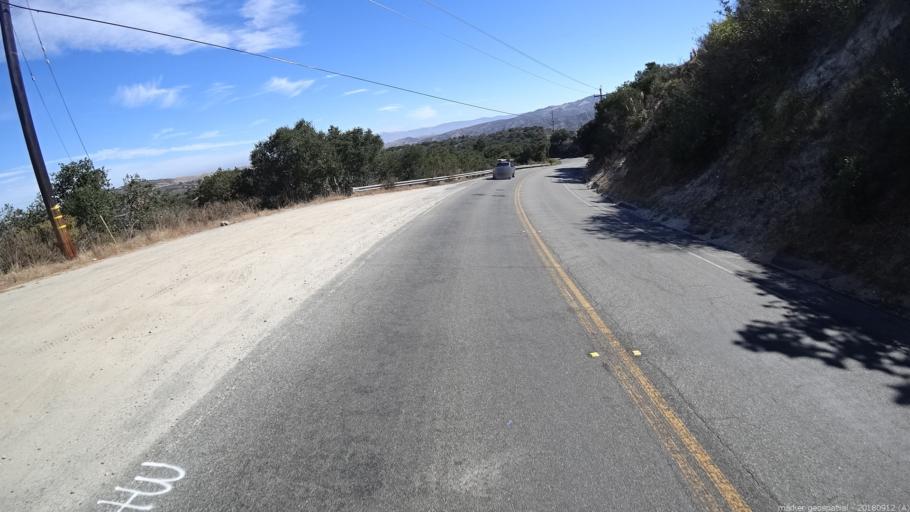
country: US
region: California
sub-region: Monterey County
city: Carmel Valley Village
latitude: 36.5562
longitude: -121.7540
